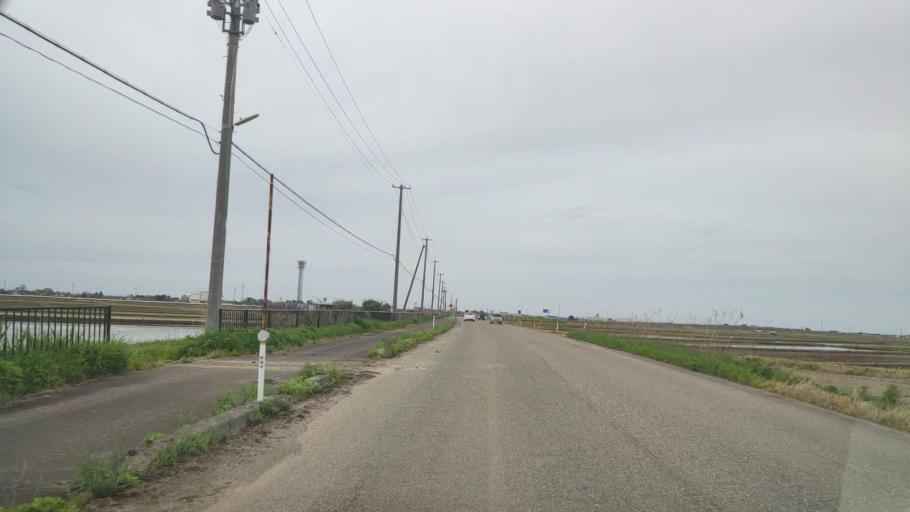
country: JP
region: Niigata
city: Shirone
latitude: 37.7340
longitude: 139.0816
